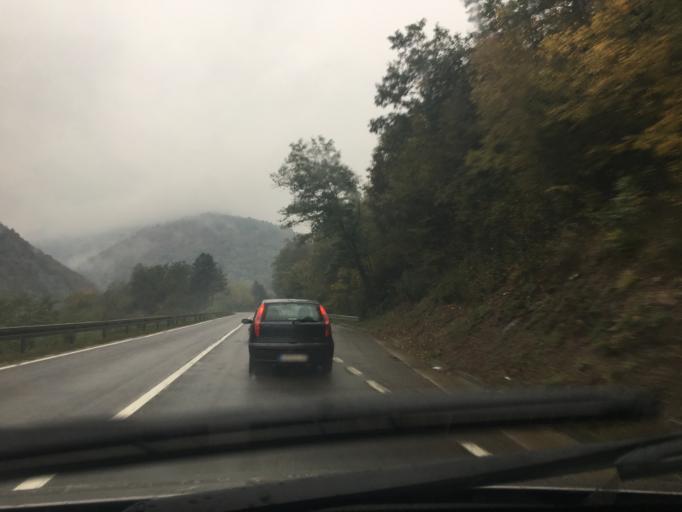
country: RS
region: Central Serbia
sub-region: Pcinjski Okrug
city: Vladicin Han
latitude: 42.7361
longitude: 22.0591
